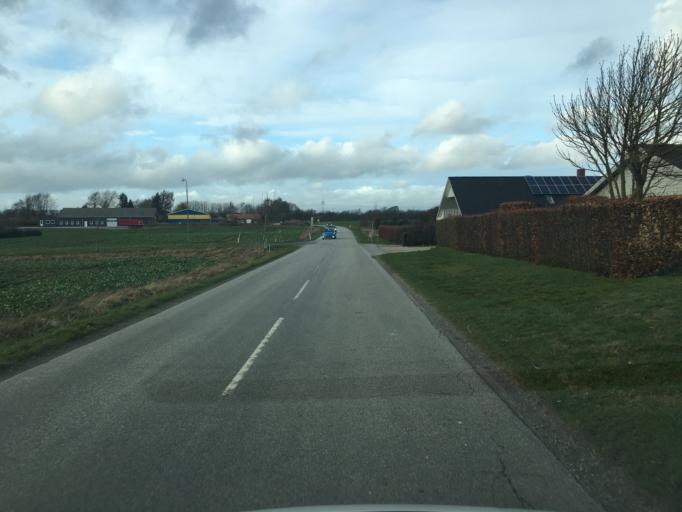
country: DK
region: South Denmark
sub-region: Sonderborg Kommune
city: Grasten
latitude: 54.9781
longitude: 9.5184
